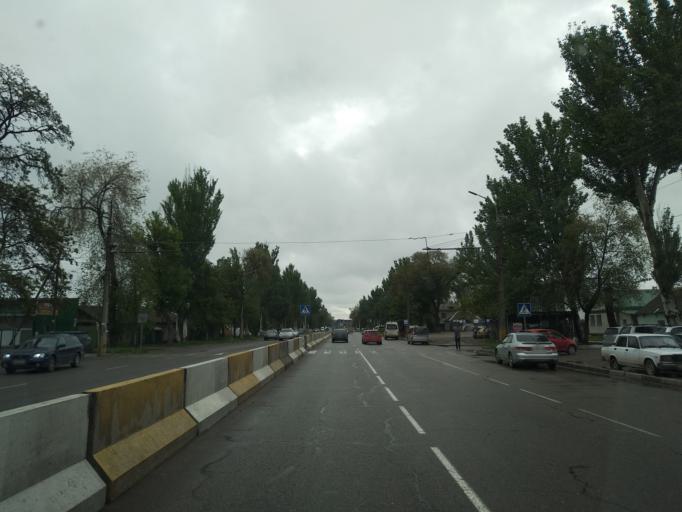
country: KG
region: Chuy
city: Lebedinovka
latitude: 42.8886
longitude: 74.6490
